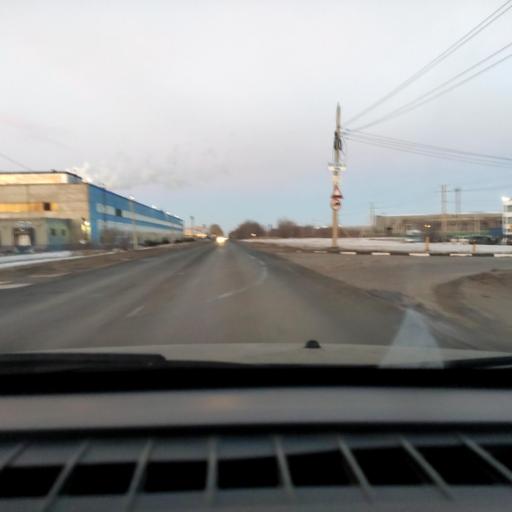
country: RU
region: Samara
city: Tol'yatti
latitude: 53.5786
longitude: 49.2840
